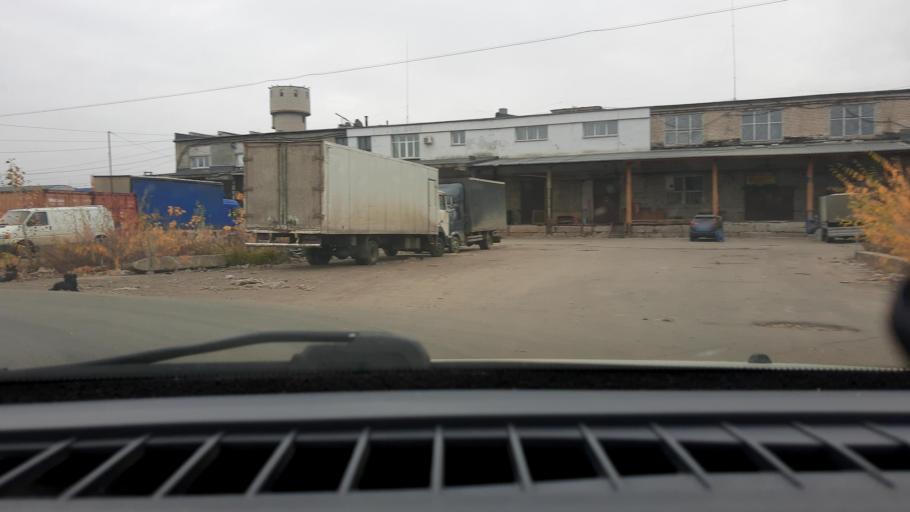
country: RU
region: Nizjnij Novgorod
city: Gorbatovka
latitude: 56.3362
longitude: 43.8110
